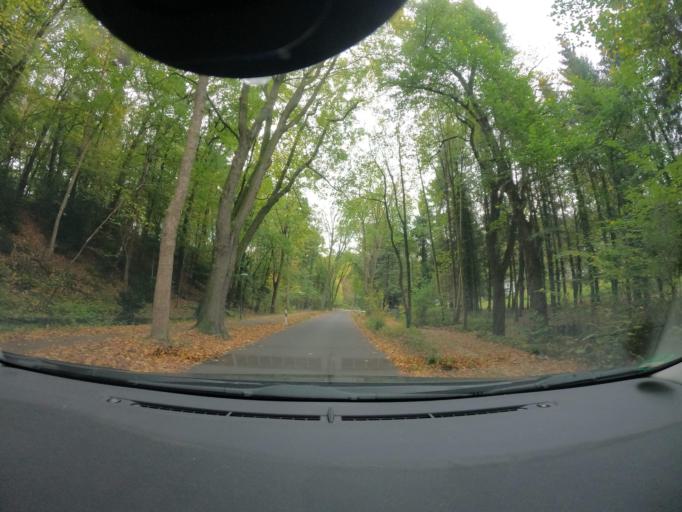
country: DE
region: North Rhine-Westphalia
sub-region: Regierungsbezirk Koln
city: Aachen
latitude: 50.7461
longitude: 6.0734
